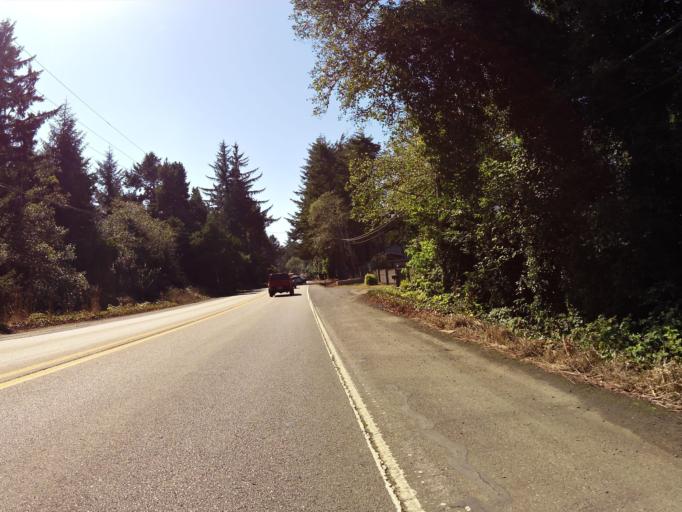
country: US
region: Oregon
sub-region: Coos County
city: Barview
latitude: 43.3495
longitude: -124.3139
